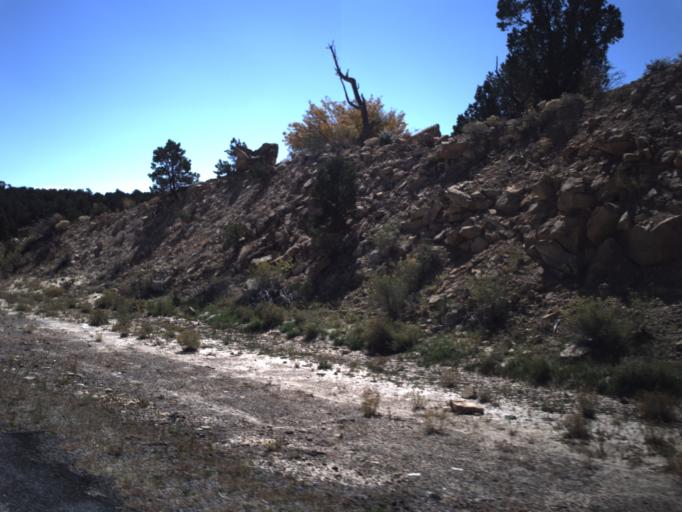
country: US
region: Utah
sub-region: San Juan County
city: Blanding
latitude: 37.5846
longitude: -109.8935
